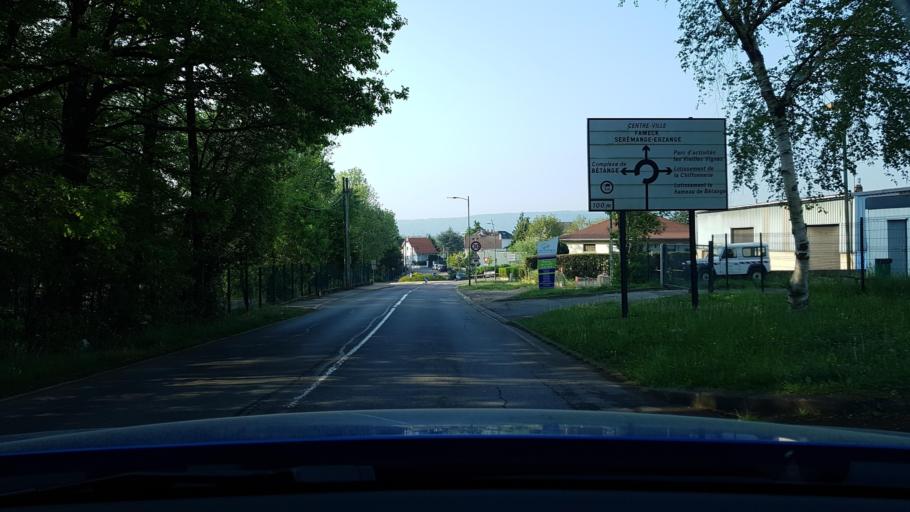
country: FR
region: Lorraine
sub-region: Departement de la Moselle
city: Florange
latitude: 49.3348
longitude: 6.1130
